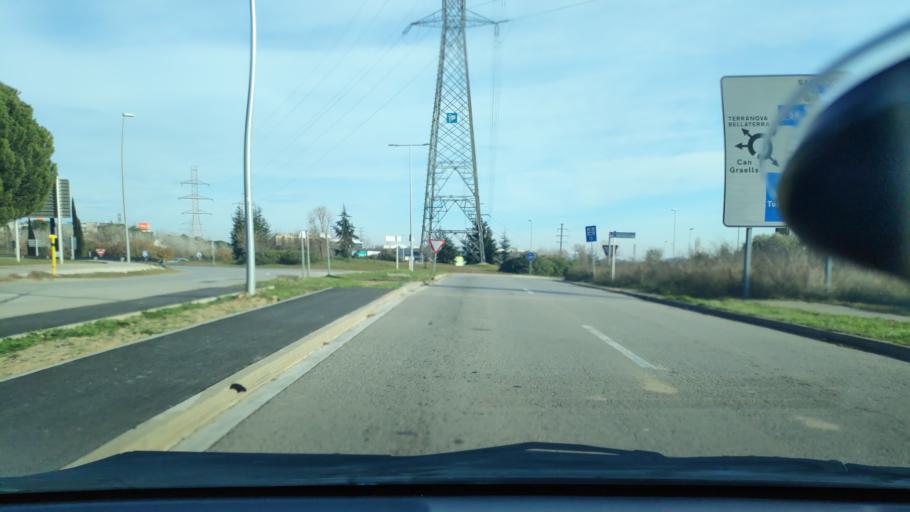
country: ES
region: Catalonia
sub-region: Provincia de Barcelona
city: Sant Cugat del Valles
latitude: 41.4904
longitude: 2.0664
